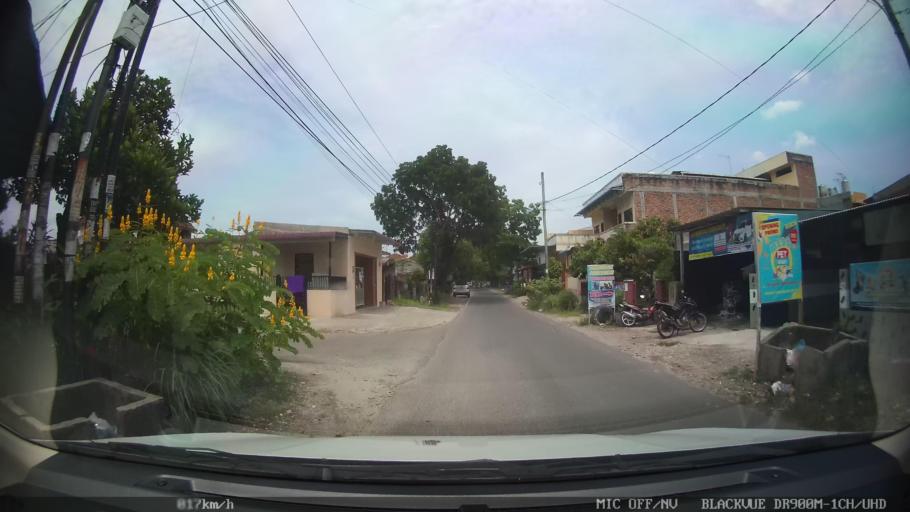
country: ID
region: North Sumatra
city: Medan
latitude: 3.5551
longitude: 98.6584
